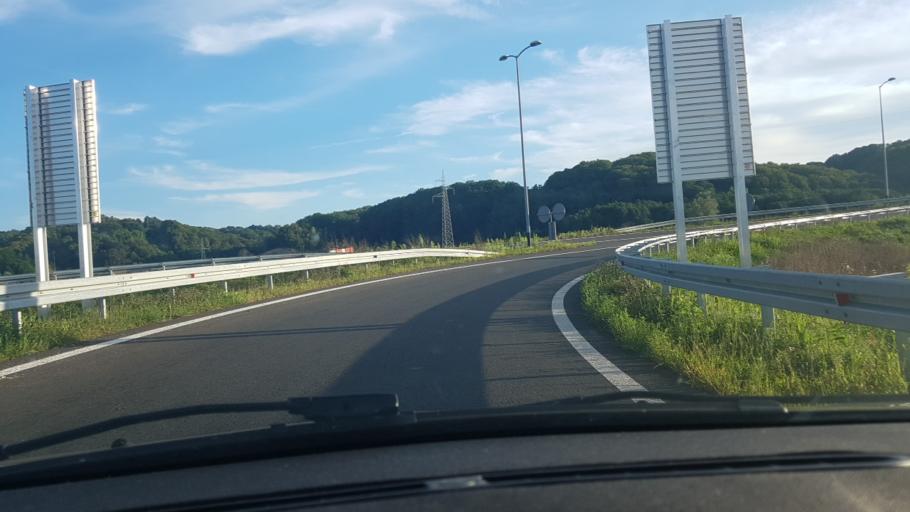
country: HR
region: Krapinsko-Zagorska
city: Selnica
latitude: 46.0368
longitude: 16.0755
